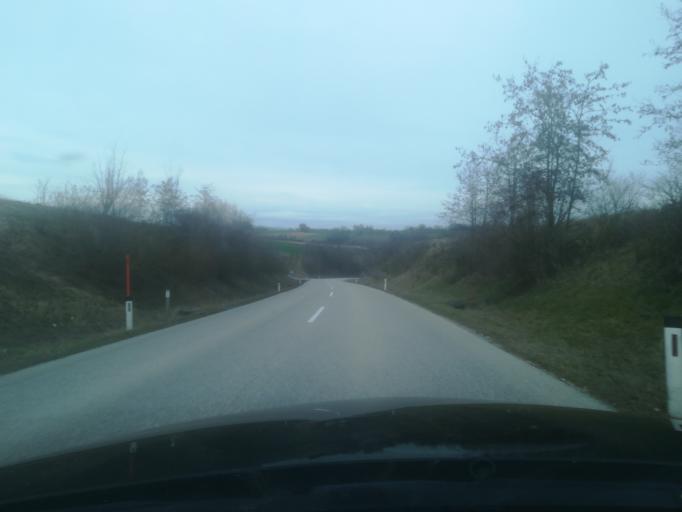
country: AT
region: Upper Austria
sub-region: Wels-Land
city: Steinhaus
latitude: 48.1248
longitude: 14.0000
